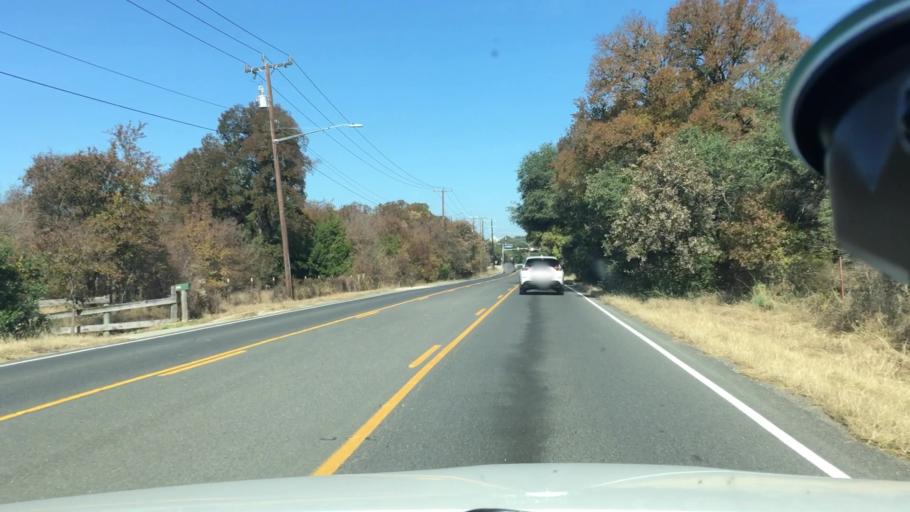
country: US
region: Texas
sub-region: Bexar County
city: Hollywood Park
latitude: 29.5905
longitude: -98.4239
